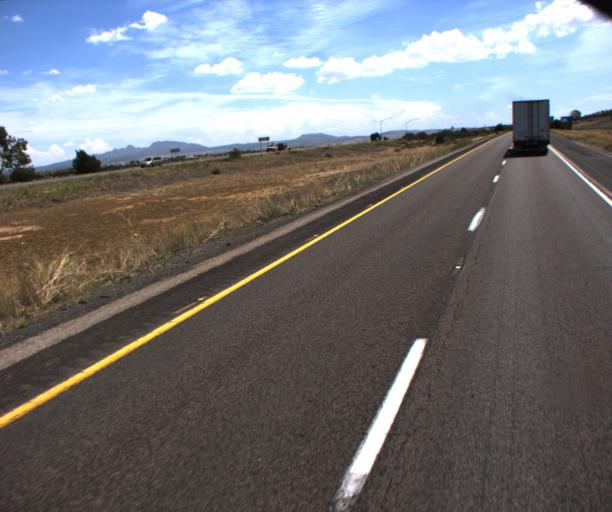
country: US
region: Arizona
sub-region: Mohave County
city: Peach Springs
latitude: 35.3214
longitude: -112.9019
